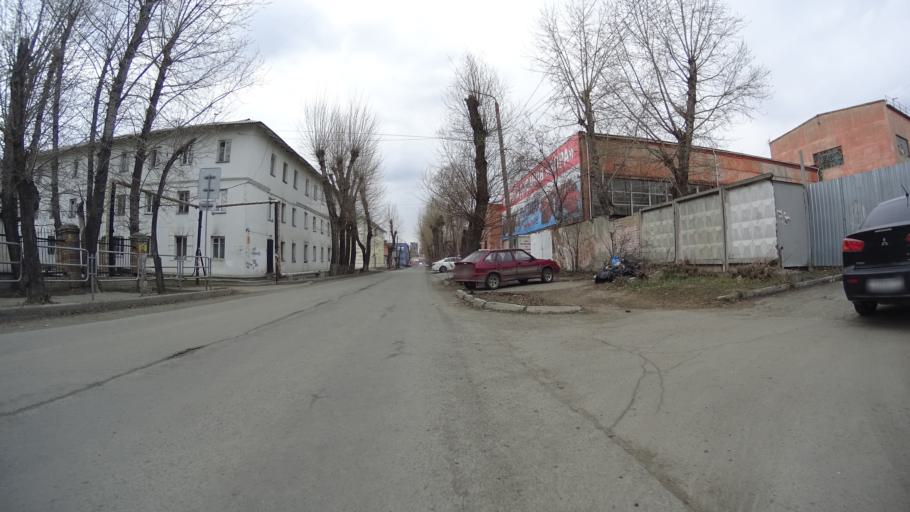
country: RU
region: Chelyabinsk
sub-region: Gorod Chelyabinsk
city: Chelyabinsk
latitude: 55.1657
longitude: 61.4373
